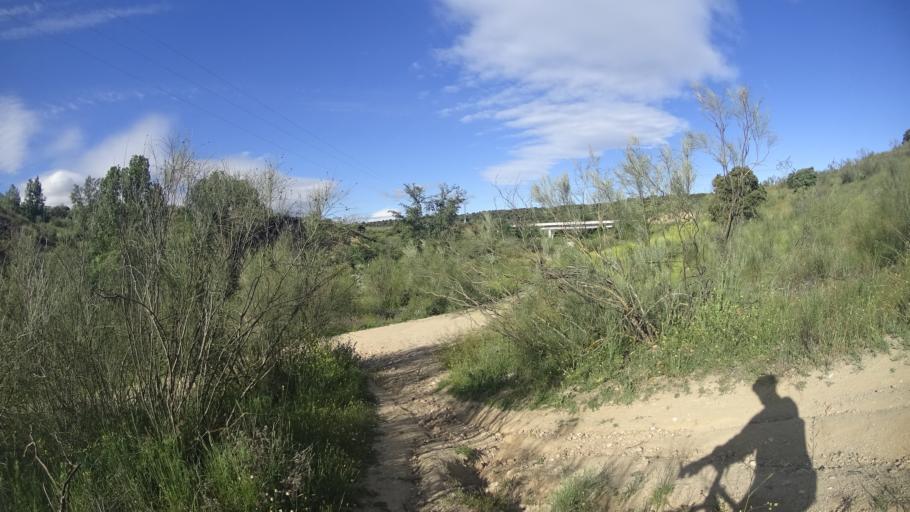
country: ES
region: Madrid
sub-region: Provincia de Madrid
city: Villanueva del Pardillo
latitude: 40.5219
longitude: -3.9358
